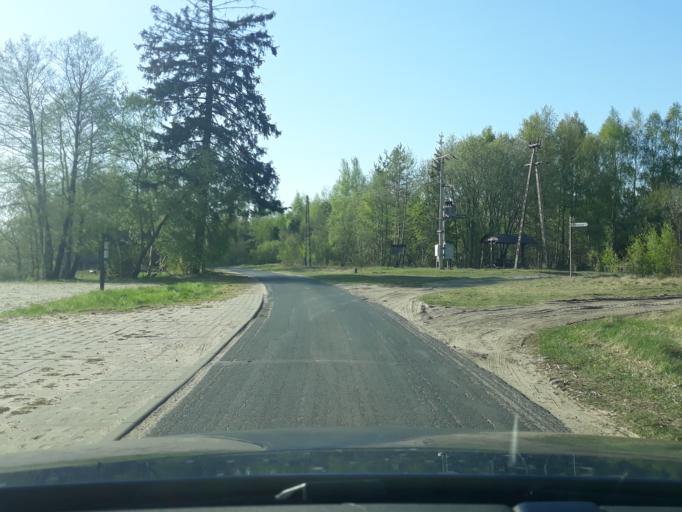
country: PL
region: Pomeranian Voivodeship
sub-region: Powiat czluchowski
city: Przechlewo
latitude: 53.8756
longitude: 17.3293
